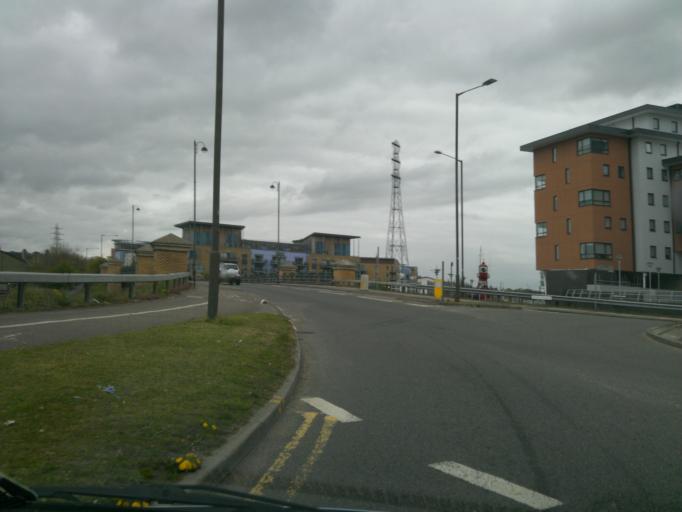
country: GB
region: England
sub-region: Essex
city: Colchester
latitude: 51.8805
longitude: 0.9267
